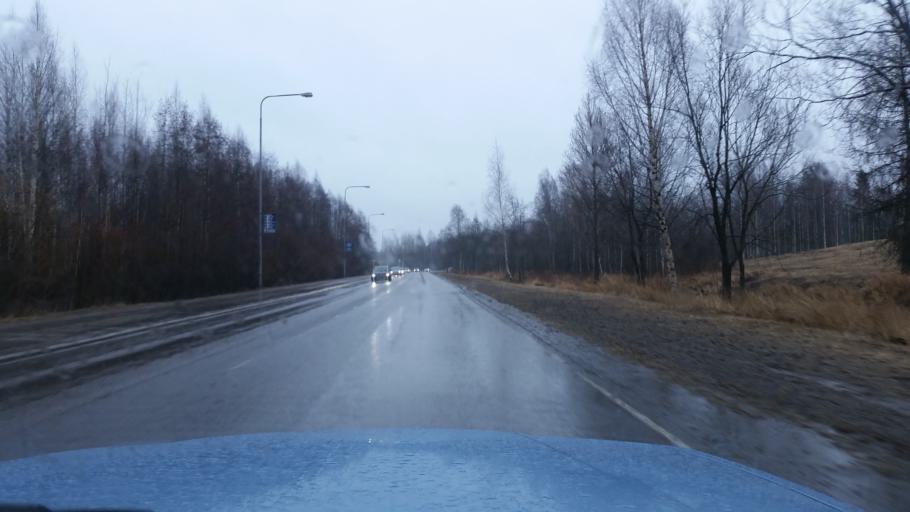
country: FI
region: Pirkanmaa
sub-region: Tampere
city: Tampere
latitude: 61.4750
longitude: 23.7852
